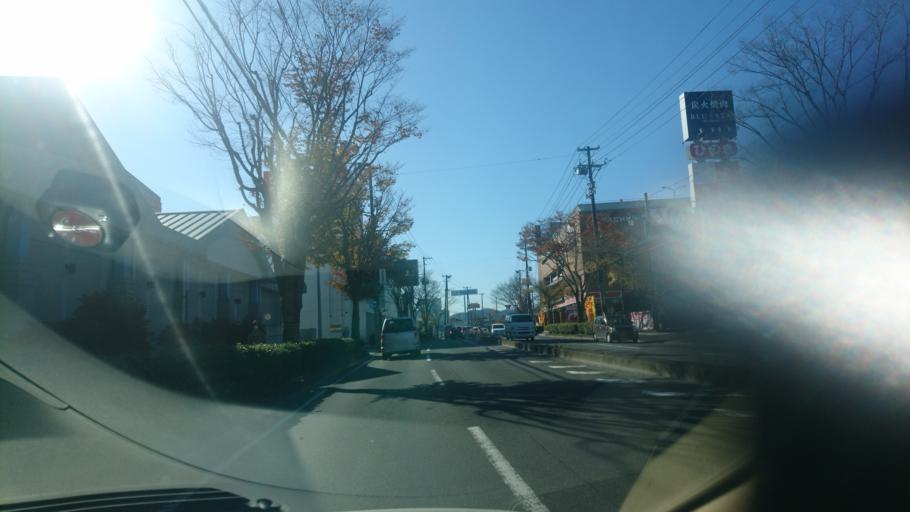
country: JP
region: Miyagi
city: Sendai-shi
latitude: 38.2871
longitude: 140.8194
